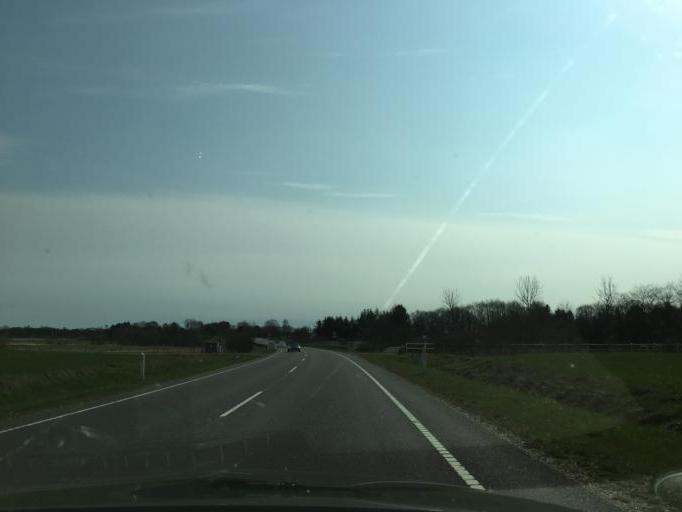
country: DK
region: South Denmark
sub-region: Vejen Kommune
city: Vejen
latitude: 55.4690
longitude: 9.1779
